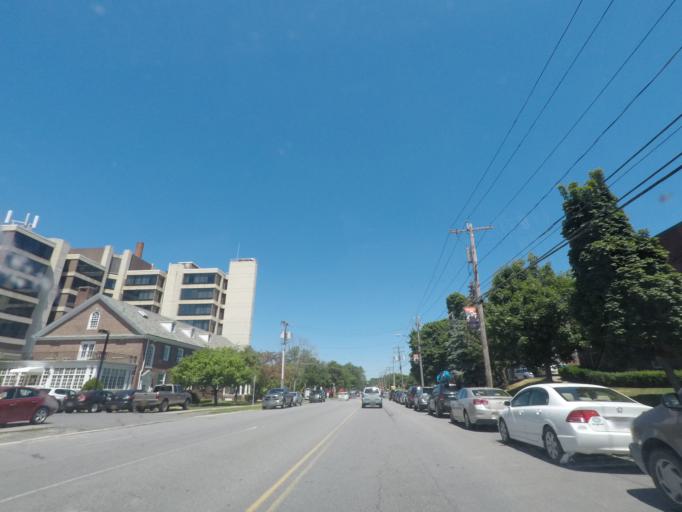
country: US
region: New York
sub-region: Rensselaer County
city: Troy
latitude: 42.7328
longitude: -73.6716
